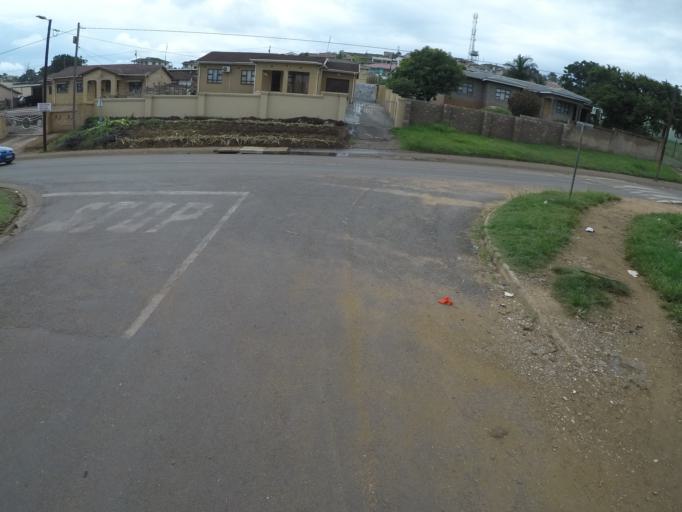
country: ZA
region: KwaZulu-Natal
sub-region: uThungulu District Municipality
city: Empangeni
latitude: -28.7828
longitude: 31.8583
